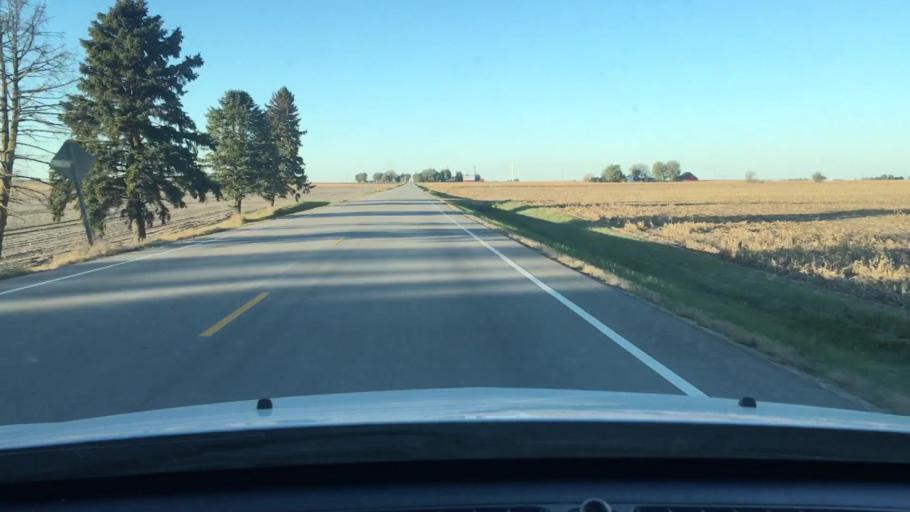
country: US
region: Illinois
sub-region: DeKalb County
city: Waterman
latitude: 41.8077
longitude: -88.8864
